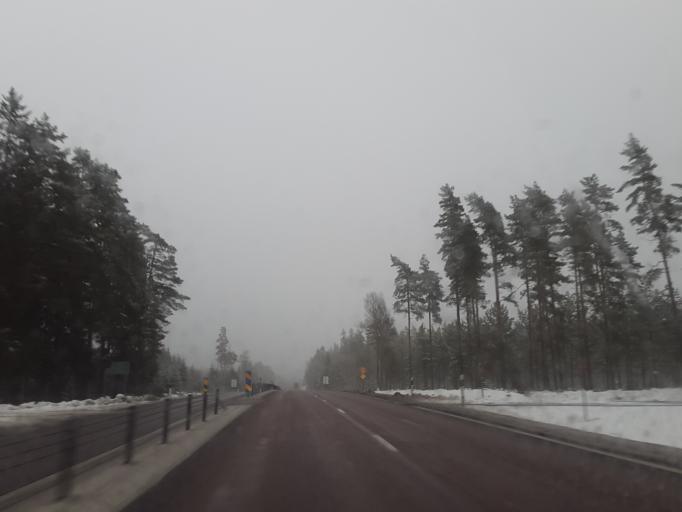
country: SE
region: Joenkoeping
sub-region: Mullsjo Kommun
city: Mullsjoe
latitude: 57.7546
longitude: 13.9192
